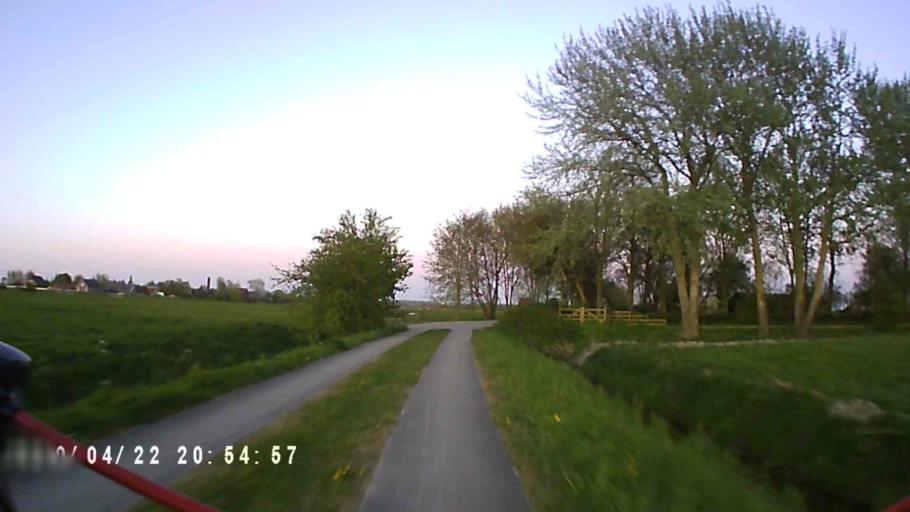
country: NL
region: Groningen
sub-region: Gemeente Winsum
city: Winsum
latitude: 53.3324
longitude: 6.5587
